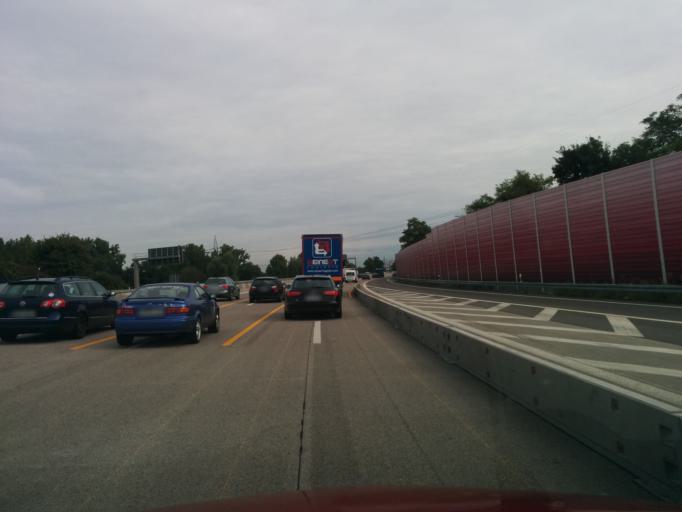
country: DE
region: Baden-Wuerttemberg
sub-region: Karlsruhe Region
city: Karlsruhe
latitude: 48.9923
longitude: 8.4366
